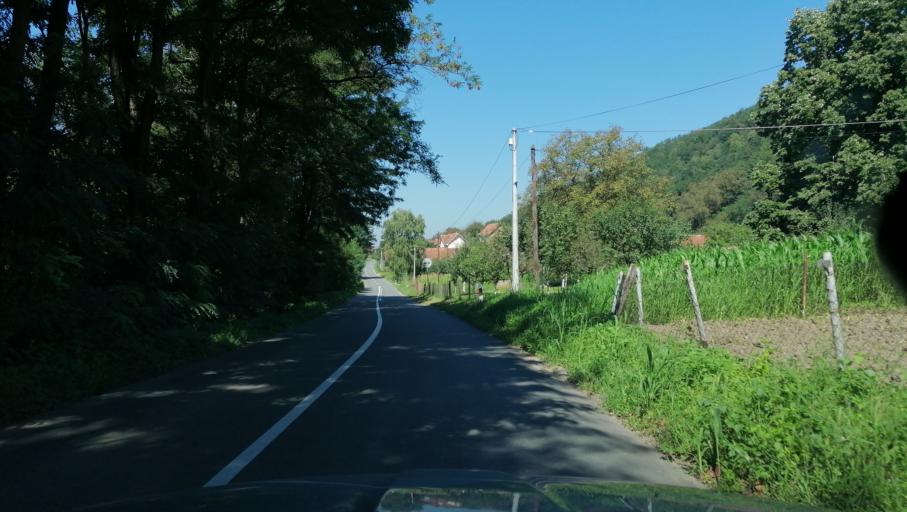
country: RS
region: Central Serbia
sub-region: Raski Okrug
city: Vrnjacka Banja
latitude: 43.6629
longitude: 20.9228
